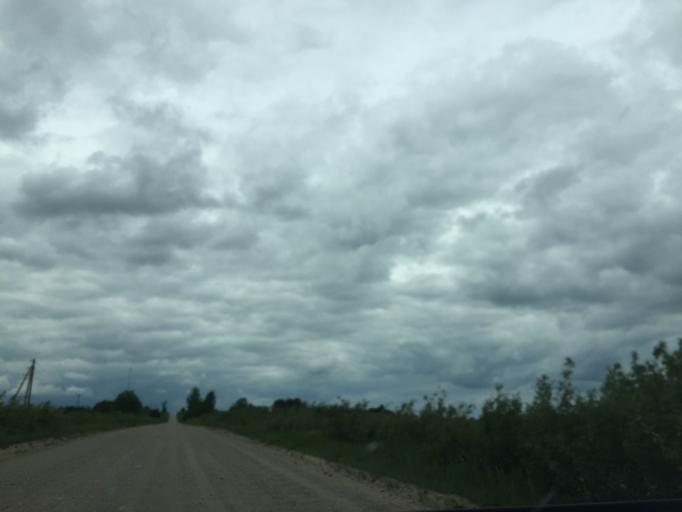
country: LV
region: Dagda
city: Dagda
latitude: 56.0082
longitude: 27.6038
